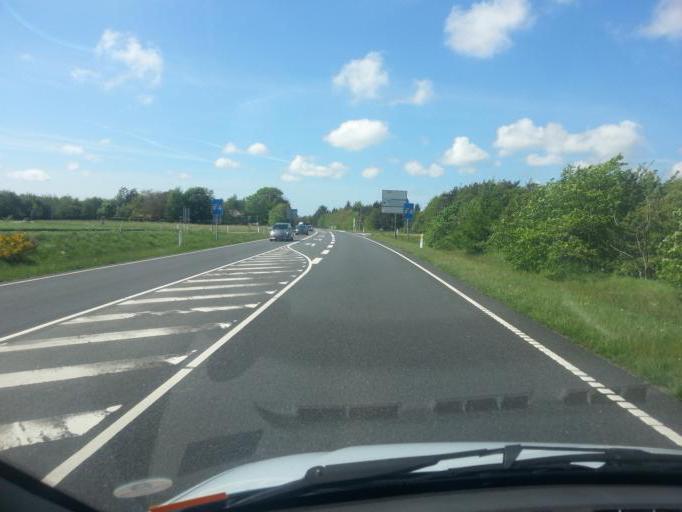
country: DK
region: South Denmark
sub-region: Varde Kommune
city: Oksbol
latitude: 55.5759
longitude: 8.3494
